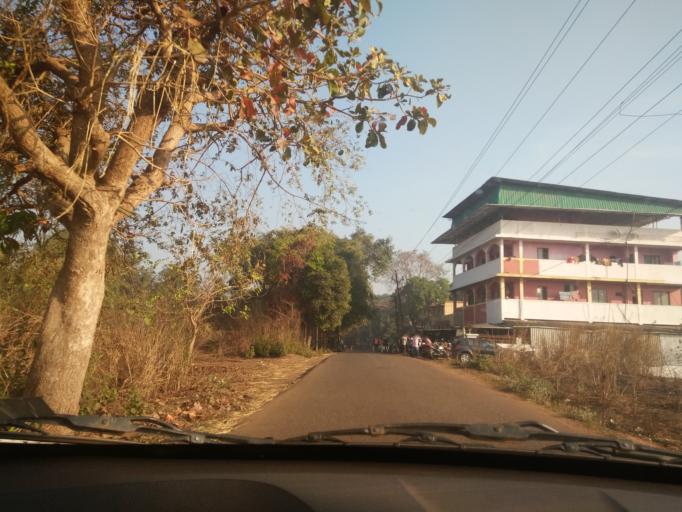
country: IN
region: Goa
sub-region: South Goa
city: Davorlim
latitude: 15.2774
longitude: 74.0057
